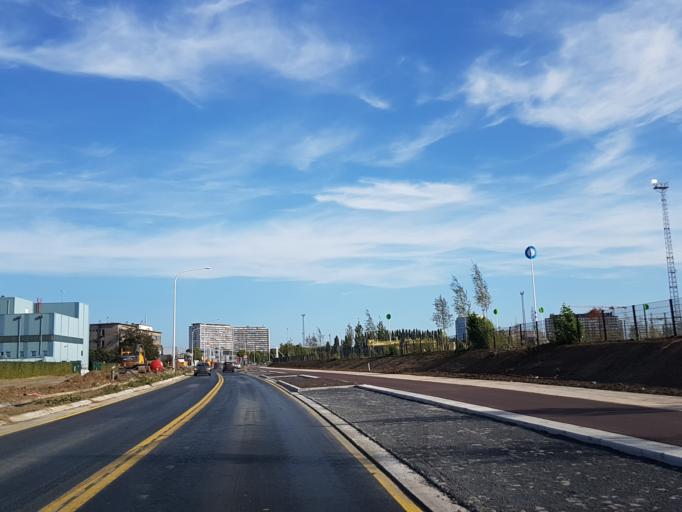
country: BE
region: Flanders
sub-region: Provincie Antwerpen
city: Antwerpen
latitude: 51.2258
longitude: 4.4428
